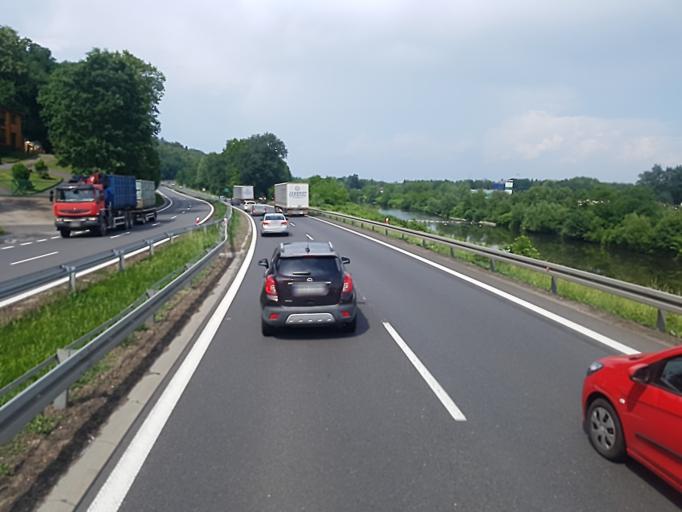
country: PL
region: Silesian Voivodeship
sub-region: Powiat cieszynski
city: Skoczow
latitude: 49.8120
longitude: 18.7917
